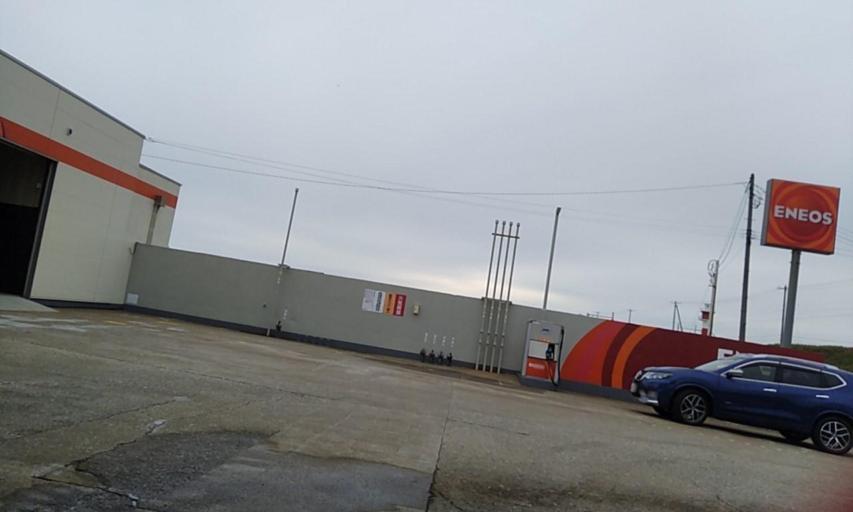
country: JP
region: Hokkaido
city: Makubetsu
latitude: 45.3493
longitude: 142.1504
